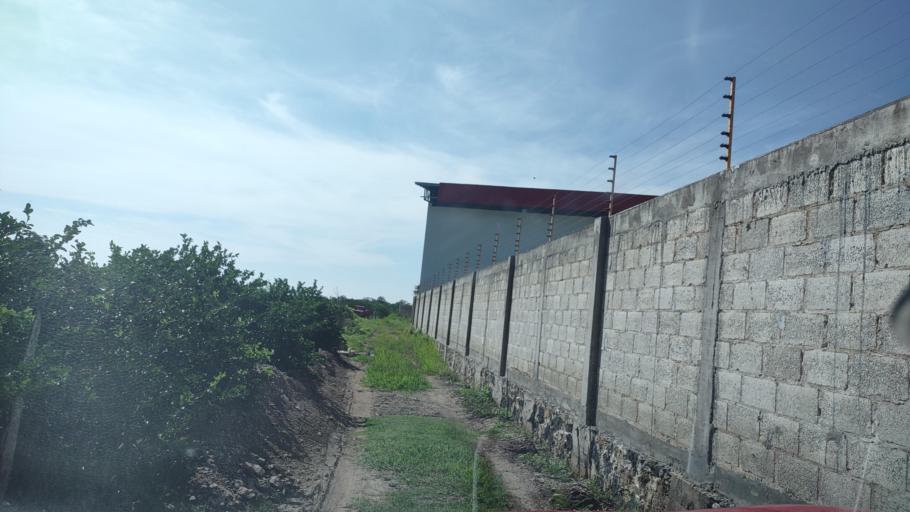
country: MX
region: Veracruz
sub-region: Emiliano Zapata
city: Dos Rios
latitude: 19.4331
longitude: -96.8019
